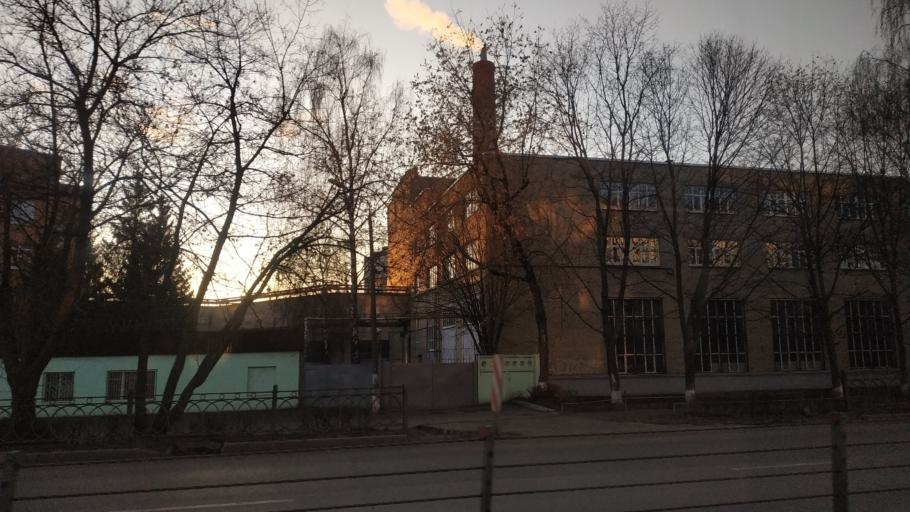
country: RU
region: Moskovskaya
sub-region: Podol'skiy Rayon
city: Podol'sk
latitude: 55.4168
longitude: 37.5751
